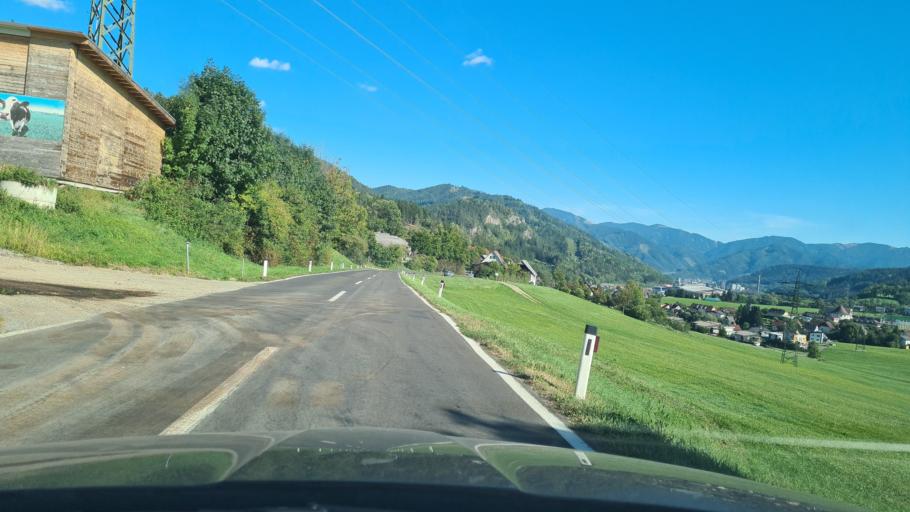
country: AT
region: Styria
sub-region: Politischer Bezirk Leoben
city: Sankt Peter-Freienstein
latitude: 47.4032
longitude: 15.0139
